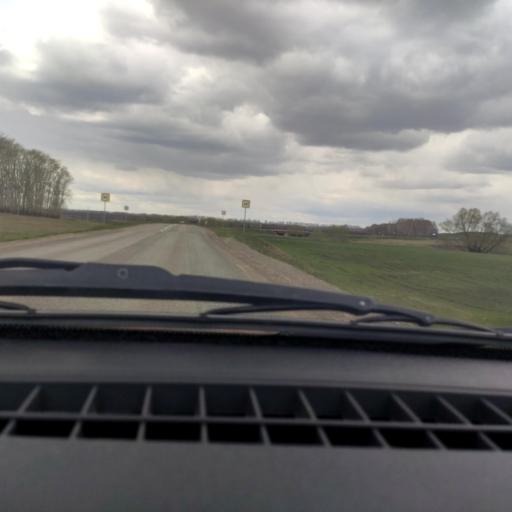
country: RU
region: Bashkortostan
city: Chekmagush
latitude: 55.1165
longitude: 54.7581
